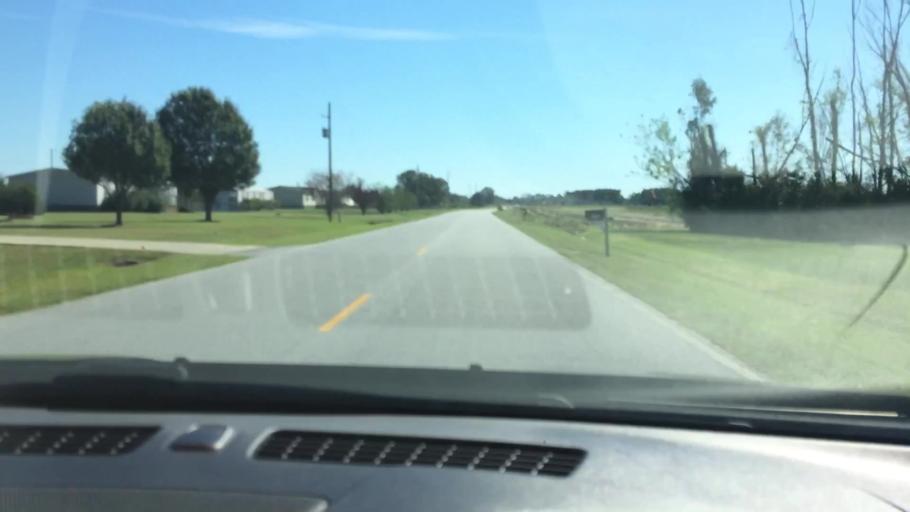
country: US
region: North Carolina
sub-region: Pitt County
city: Grifton
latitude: 35.3868
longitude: -77.3812
